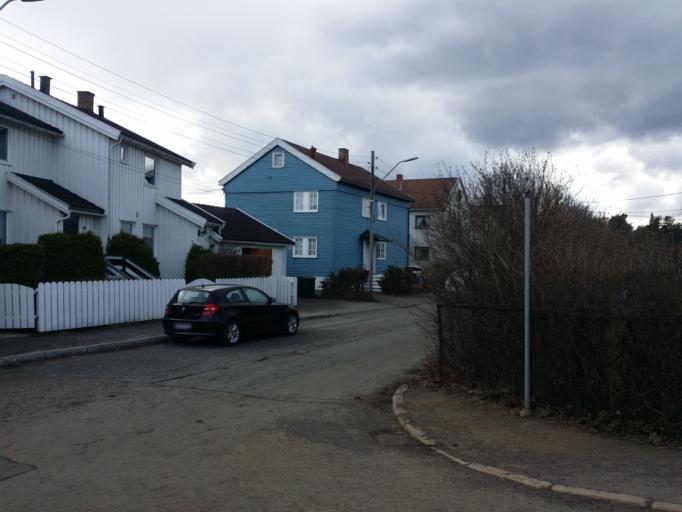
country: NO
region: Oslo
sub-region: Oslo
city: Oslo
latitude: 59.9527
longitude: 10.7854
